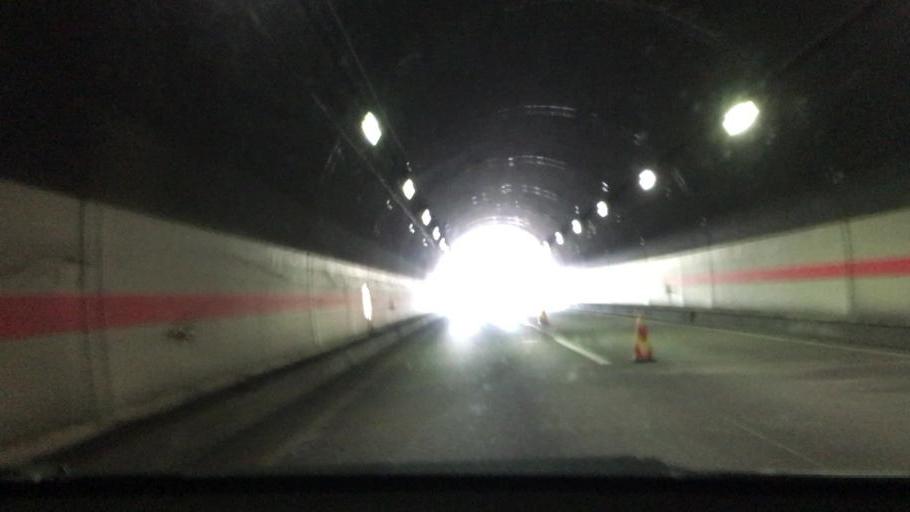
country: JP
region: Yamaguchi
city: Tokuyama
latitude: 34.0549
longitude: 131.8405
